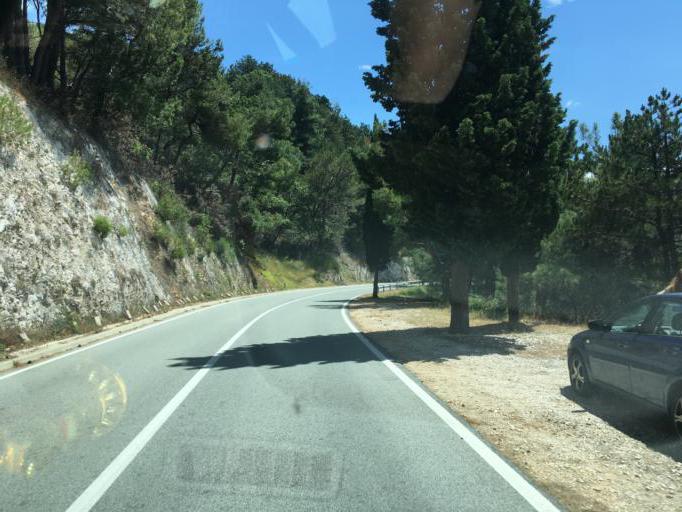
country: HR
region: Istarska
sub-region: Grad Labin
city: Rabac
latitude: 45.1316
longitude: 14.1910
